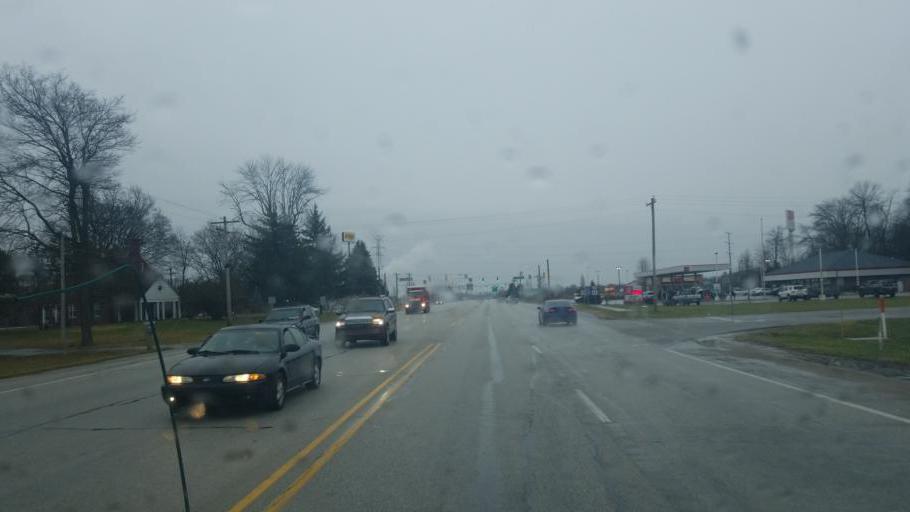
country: US
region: Indiana
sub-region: Shelby County
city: Shelbyville
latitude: 39.5554
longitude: -85.7759
